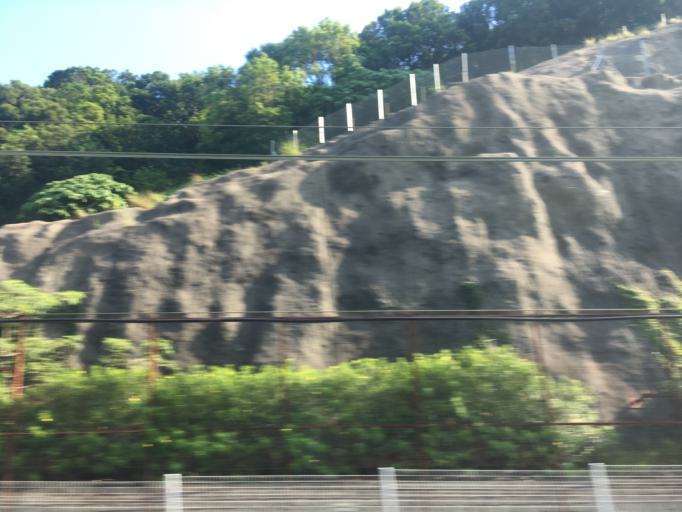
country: HK
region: Tuen Mun
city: Tuen Mun
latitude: 22.3255
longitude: 114.0139
